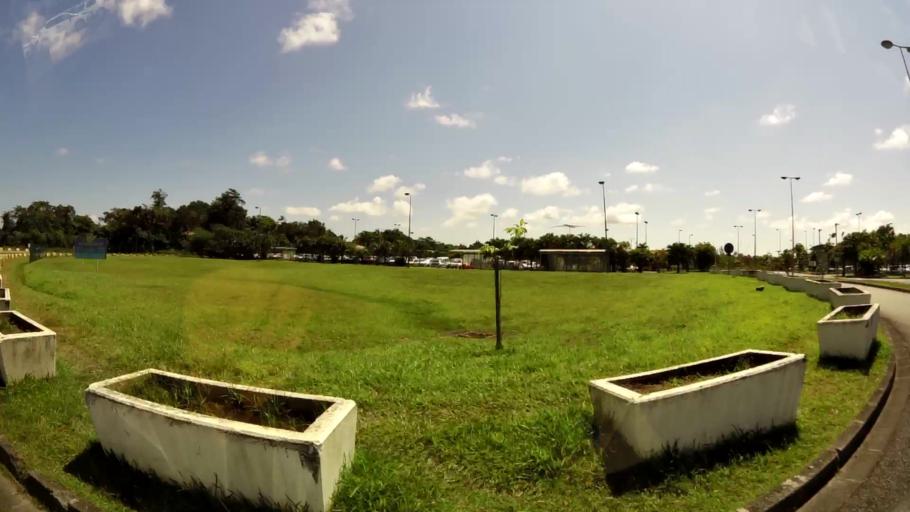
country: GF
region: Guyane
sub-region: Guyane
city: Matoury
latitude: 4.8238
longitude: -52.3648
